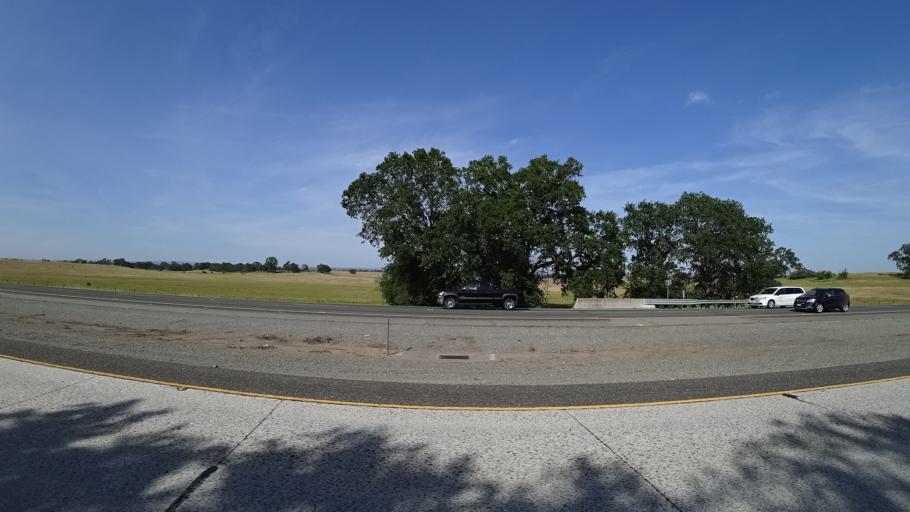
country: US
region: California
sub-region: Butte County
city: Durham
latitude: 39.6846
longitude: -121.7674
